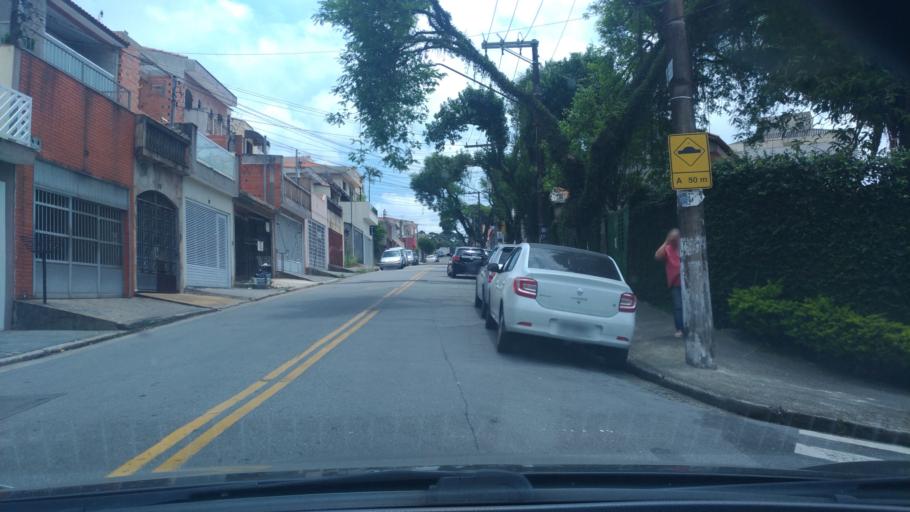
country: BR
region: Sao Paulo
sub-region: Sao Bernardo Do Campo
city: Sao Bernardo do Campo
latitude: -23.7183
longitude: -46.5625
